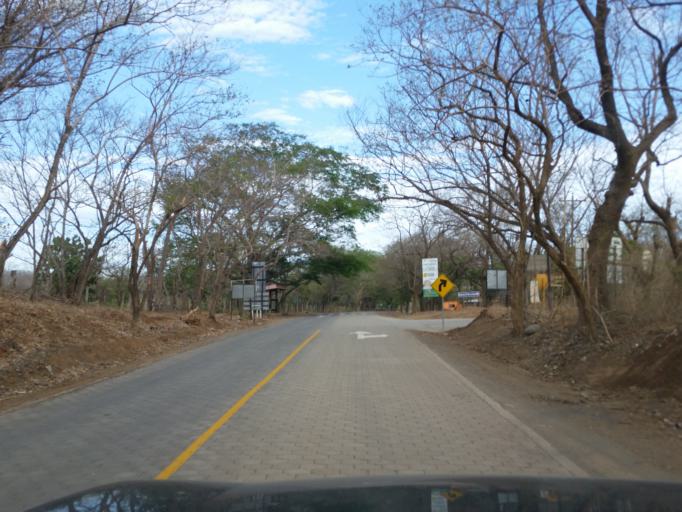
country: NI
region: Rivas
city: Tola
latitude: 11.4010
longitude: -85.9961
